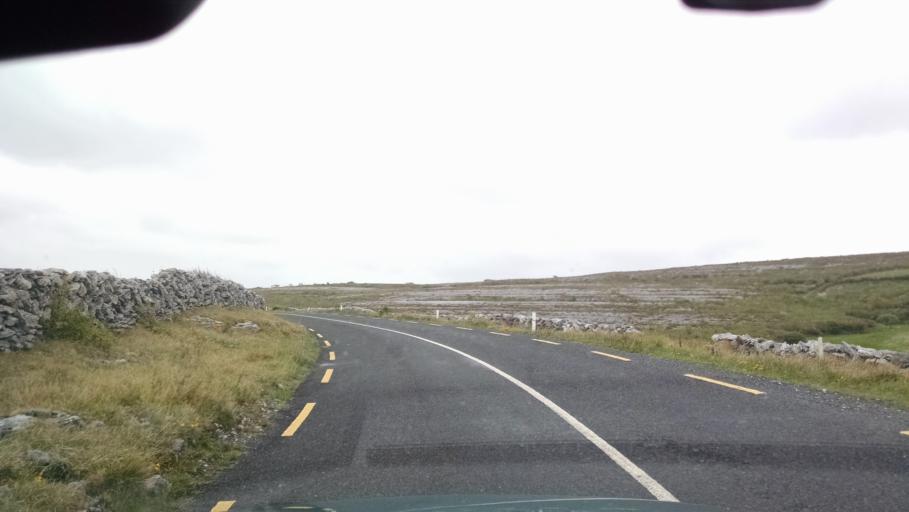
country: IE
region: Connaught
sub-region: County Galway
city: Bearna
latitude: 53.0786
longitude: -9.1641
